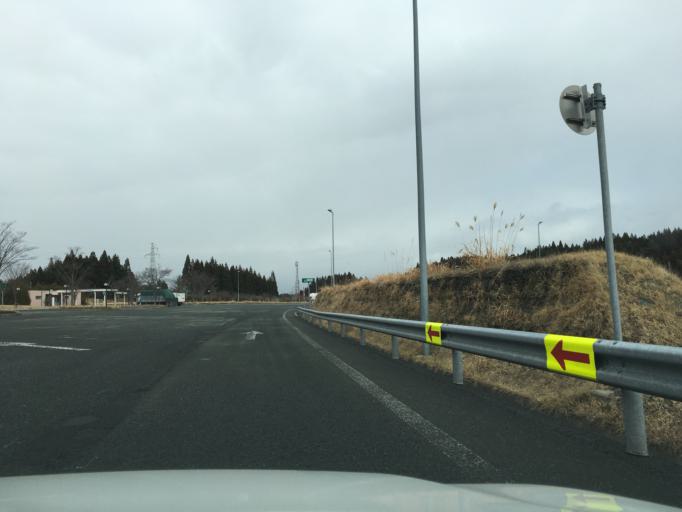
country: JP
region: Akita
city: Tenno
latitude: 40.0084
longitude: 140.0874
